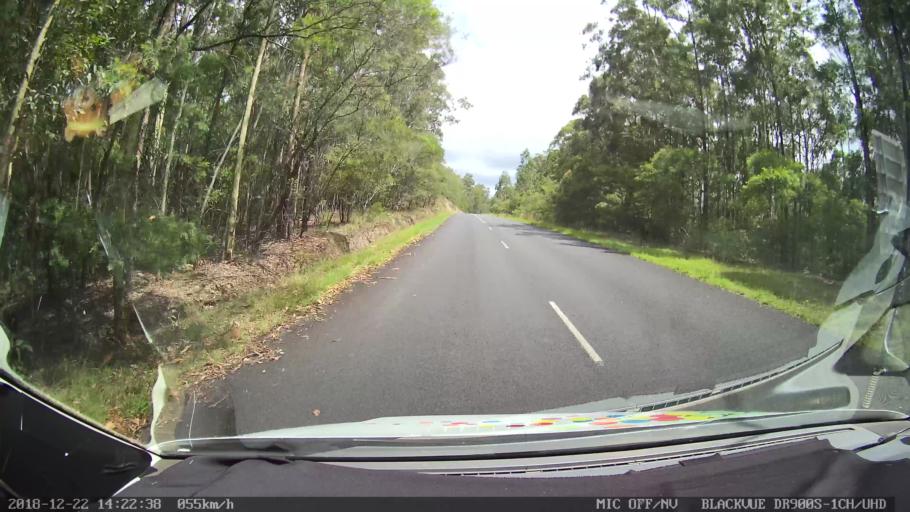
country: AU
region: New South Wales
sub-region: Clarence Valley
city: Coutts Crossing
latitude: -30.0275
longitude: 152.6535
